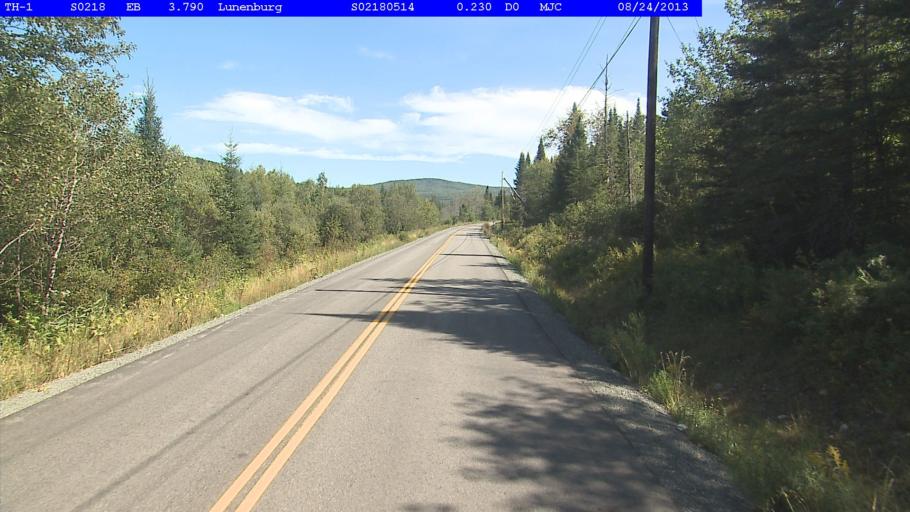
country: US
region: New Hampshire
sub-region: Grafton County
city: Littleton
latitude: 44.4194
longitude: -71.7432
